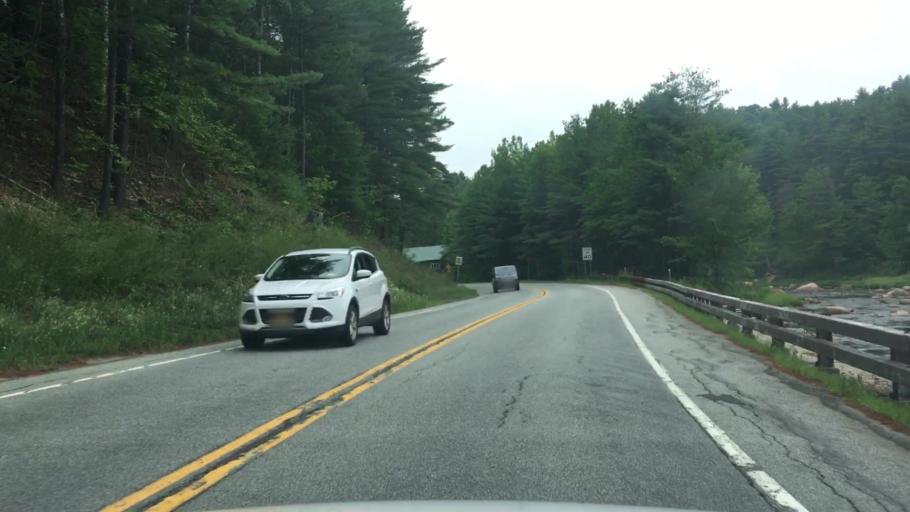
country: US
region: New York
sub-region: Essex County
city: Keeseville
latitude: 44.4278
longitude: -73.6799
